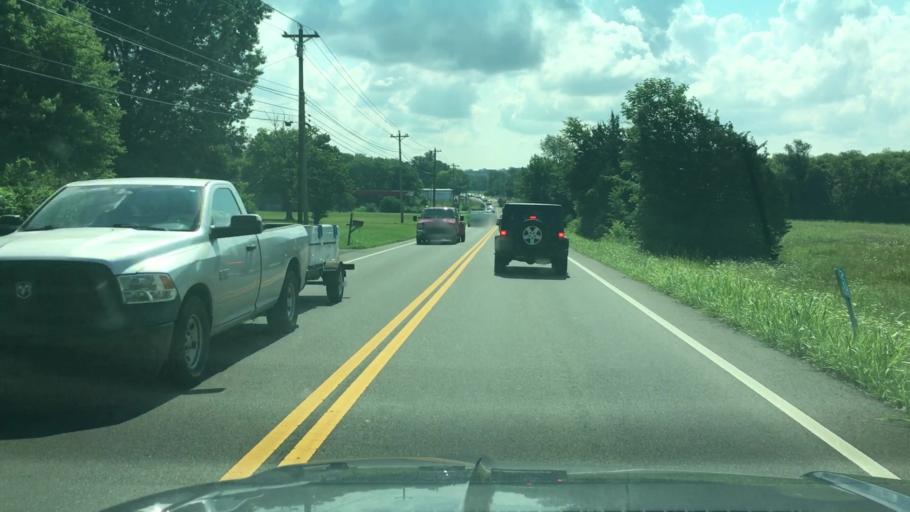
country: US
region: Tennessee
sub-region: Williamson County
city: Nolensville
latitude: 35.8684
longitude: -86.7148
